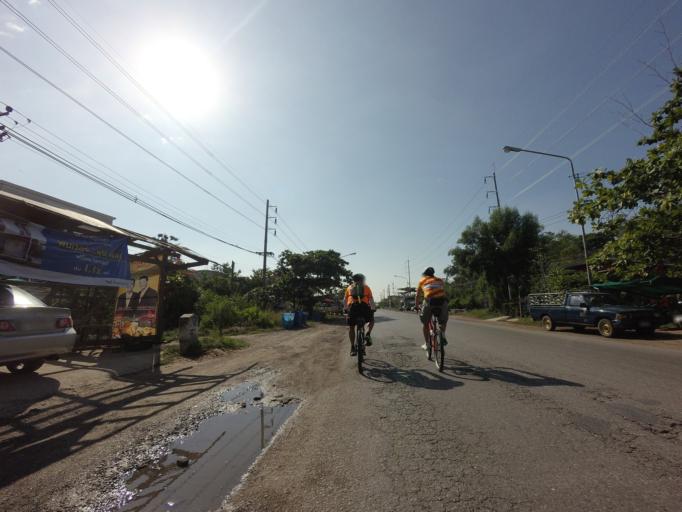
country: TH
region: Samut Prakan
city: Phra Samut Chedi
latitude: 13.5913
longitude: 100.5802
